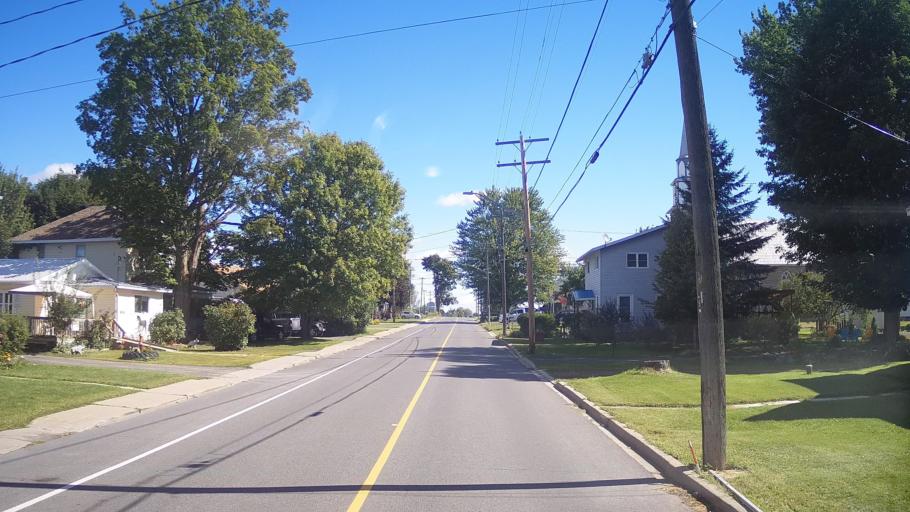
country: US
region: New York
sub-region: St. Lawrence County
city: Norfolk
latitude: 44.9764
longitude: -75.2405
